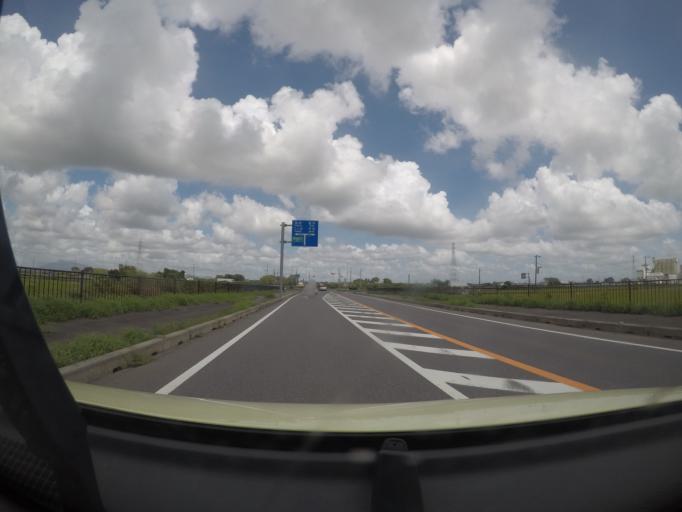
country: JP
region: Ibaraki
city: Mitsukaido
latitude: 36.0657
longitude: 139.9891
